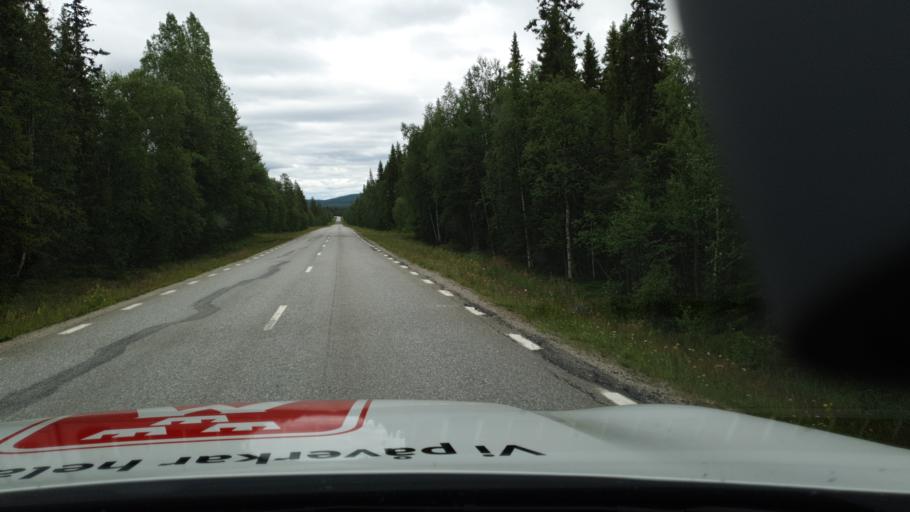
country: SE
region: Vaesterbotten
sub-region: Lycksele Kommun
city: Soderfors
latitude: 64.7069
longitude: 17.7178
